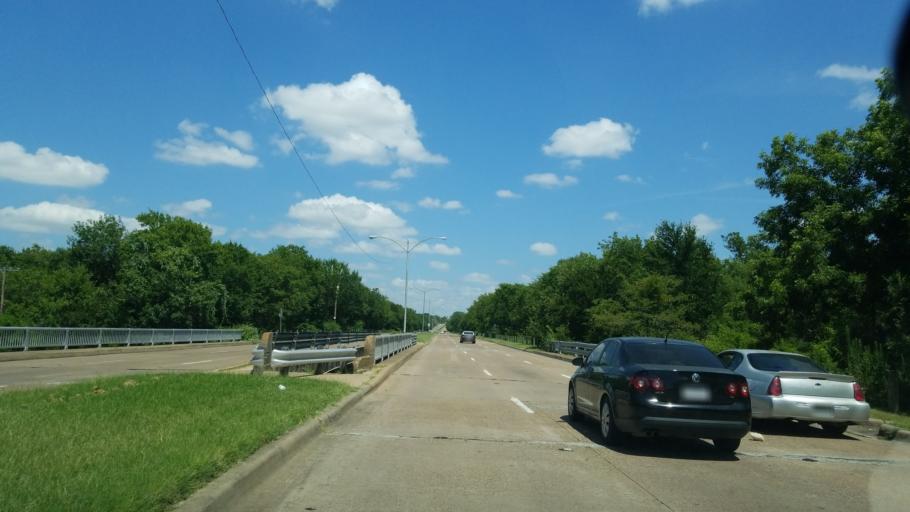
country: US
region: Texas
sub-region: Dallas County
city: Dallas
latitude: 32.7492
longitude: -96.7178
